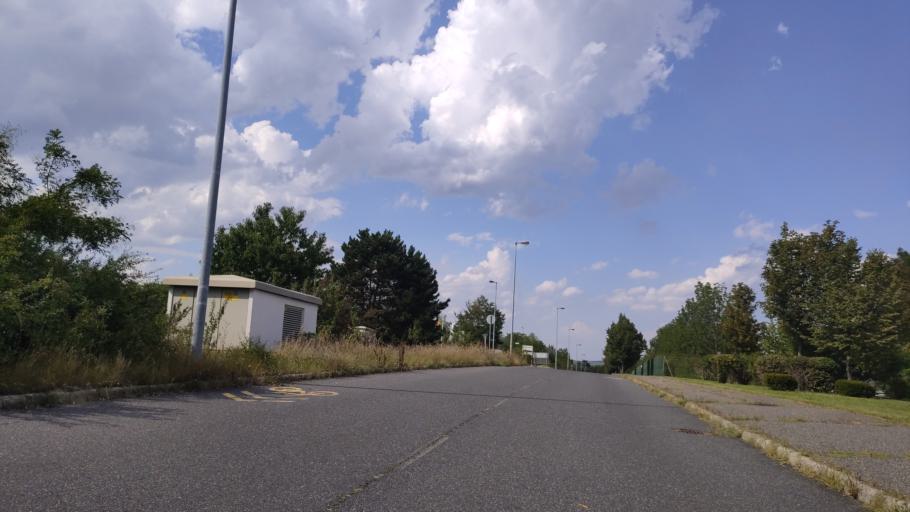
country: HU
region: Pest
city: Toeroekbalint
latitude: 47.4437
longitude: 18.8819
